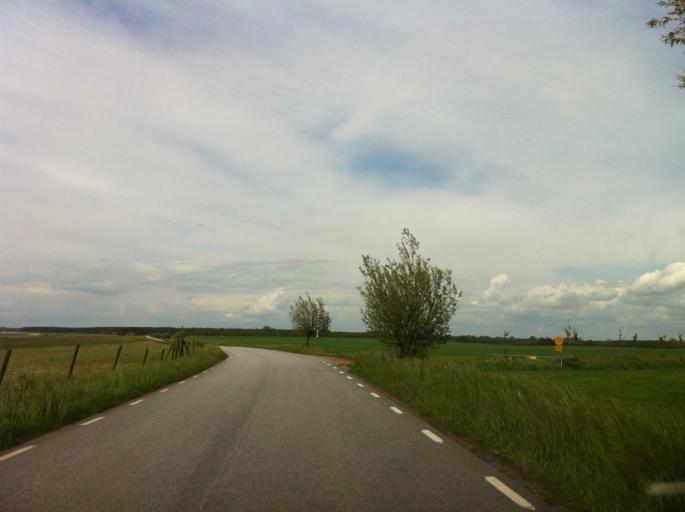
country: SE
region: Skane
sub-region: Kavlinge Kommun
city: Hofterup
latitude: 55.7733
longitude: 12.9319
